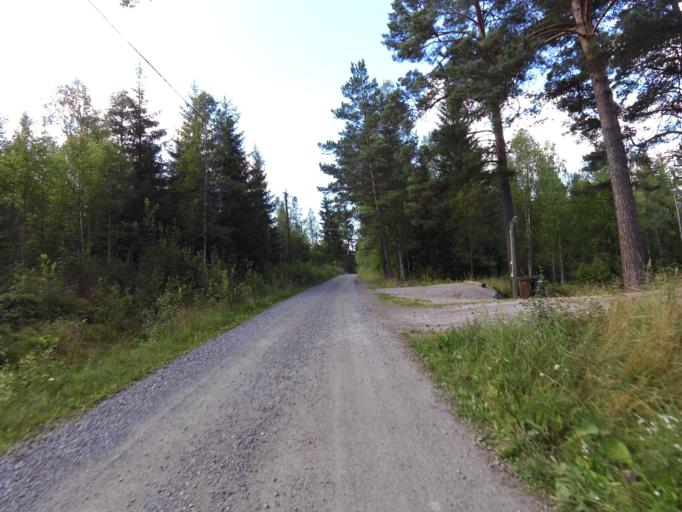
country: SE
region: Dalarna
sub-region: Faluns Kommun
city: Svardsjo
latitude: 60.6909
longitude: 15.8876
